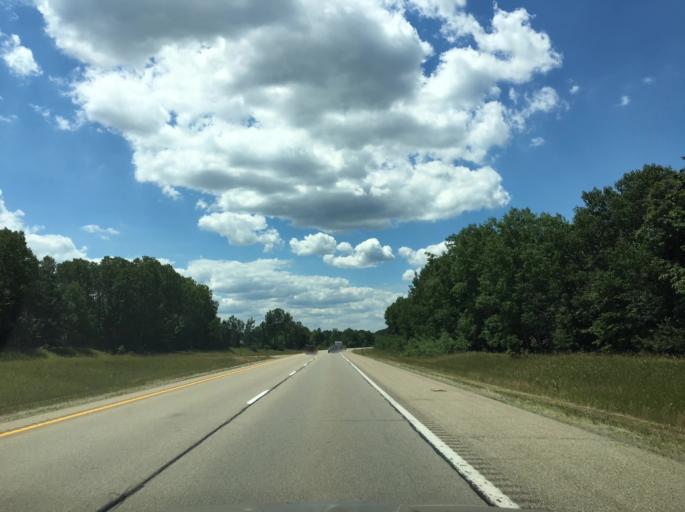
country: US
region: Michigan
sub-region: Clare County
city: Clare
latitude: 43.8785
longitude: -84.8173
